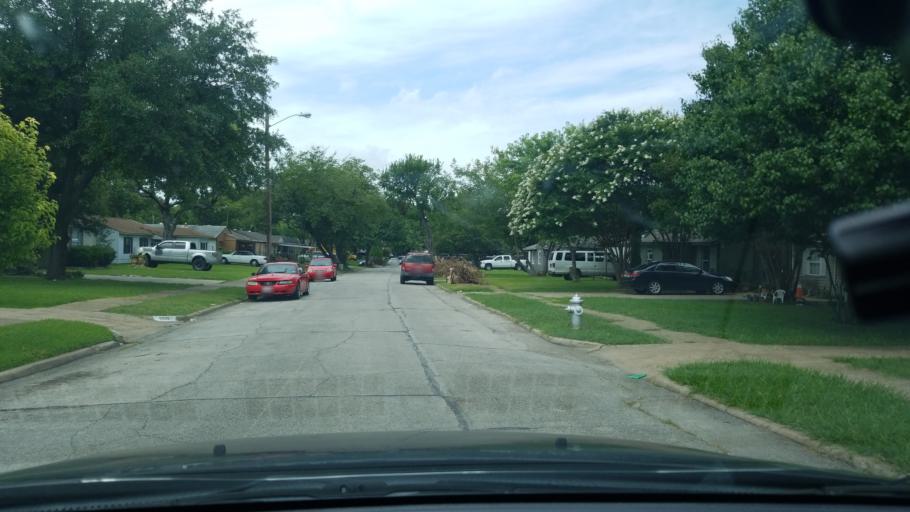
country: US
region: Texas
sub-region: Dallas County
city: Mesquite
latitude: 32.8227
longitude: -96.6721
